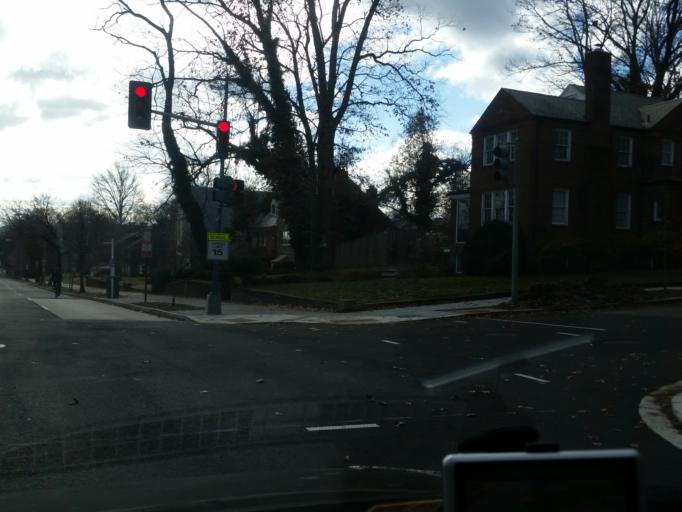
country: US
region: Maryland
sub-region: Montgomery County
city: Takoma Park
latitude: 38.9420
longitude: -77.0365
